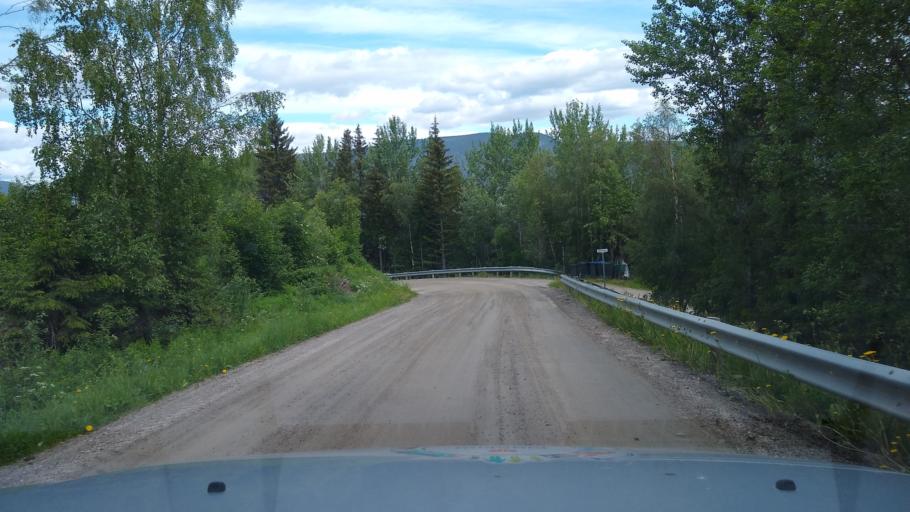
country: NO
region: Oppland
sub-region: Ringebu
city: Ringebu
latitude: 61.5099
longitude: 10.1364
